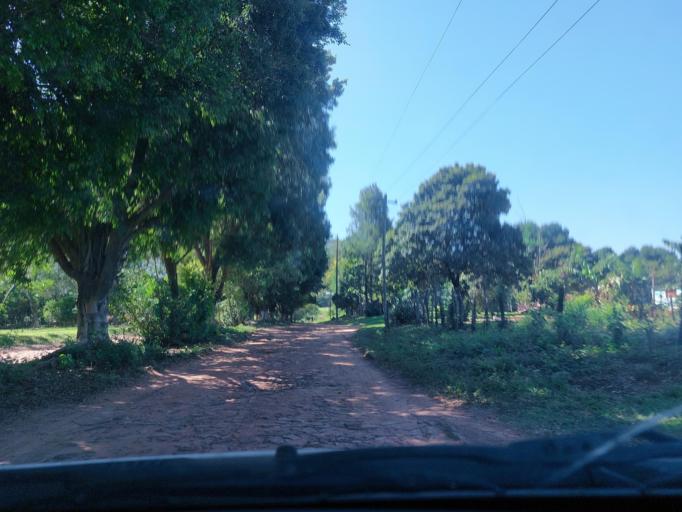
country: PY
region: San Pedro
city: Itacurubi del Rosario
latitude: -24.5571
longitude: -56.5895
